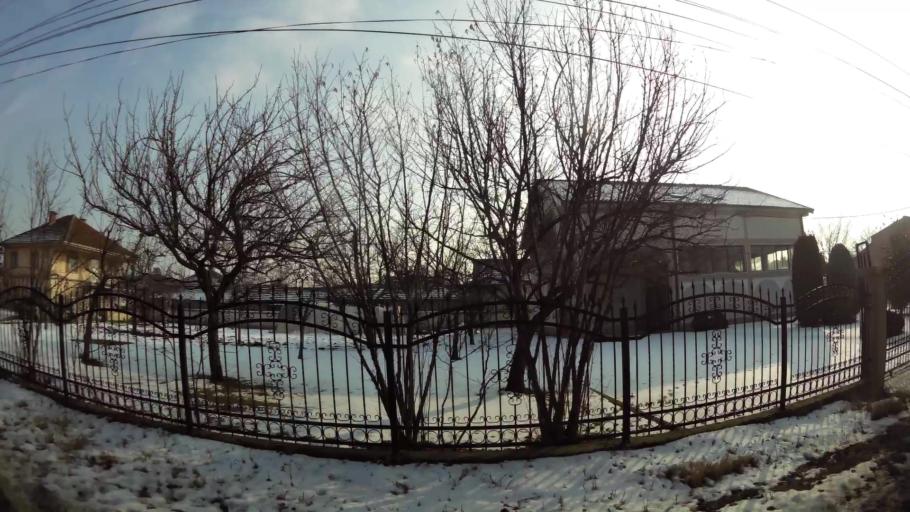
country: MK
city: Kadino
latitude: 41.9737
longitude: 21.5954
